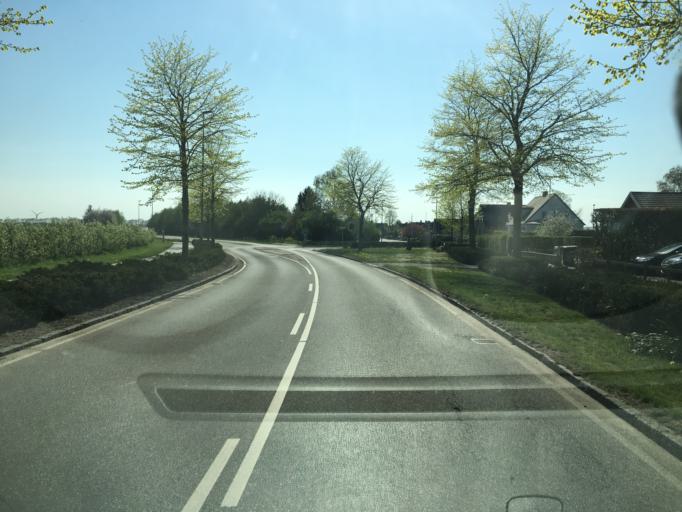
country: DK
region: South Denmark
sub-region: Haderslev Kommune
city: Vojens
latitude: 55.3175
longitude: 9.2957
